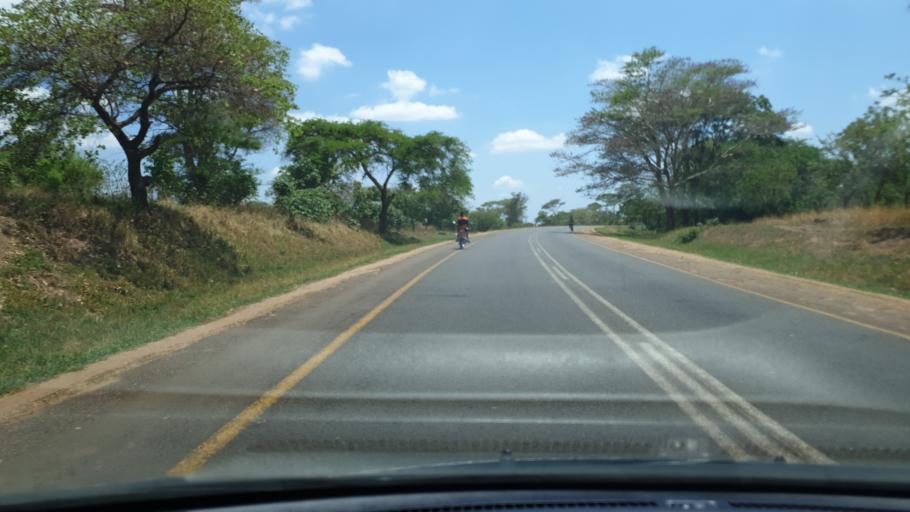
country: MW
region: Central Region
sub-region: Dowa District
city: Dowa
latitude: -13.7226
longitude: 34.0441
